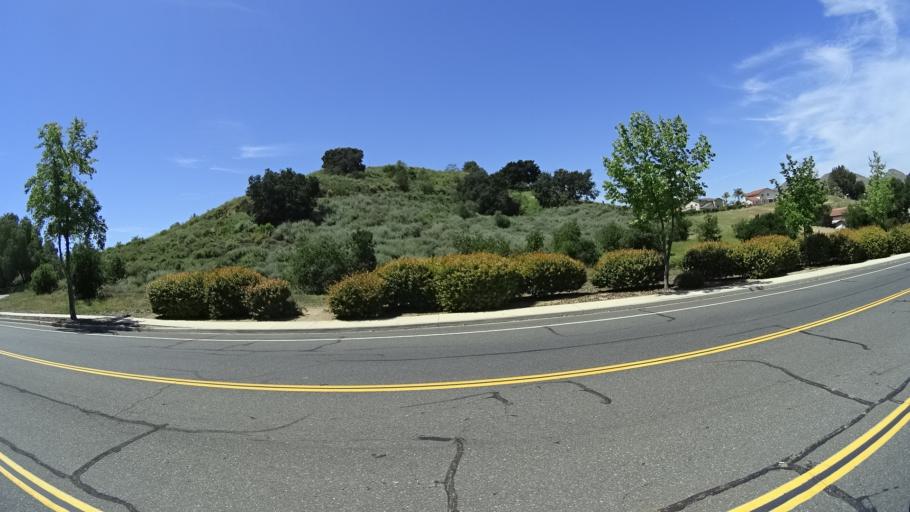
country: US
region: California
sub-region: Ventura County
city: Casa Conejo
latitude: 34.1678
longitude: -118.9432
